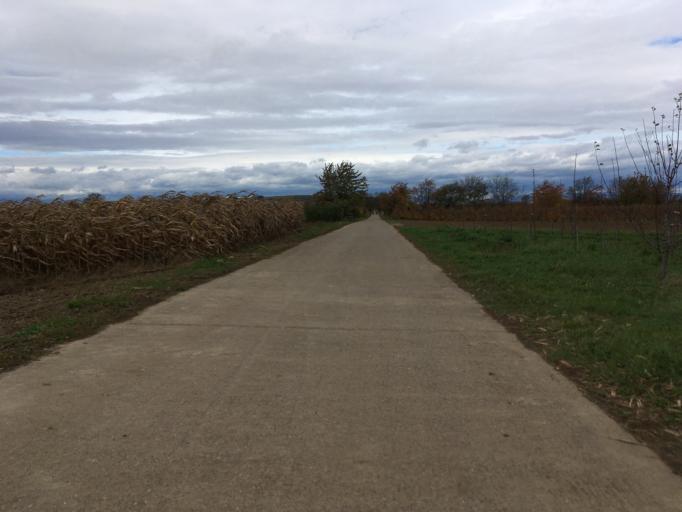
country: DE
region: Baden-Wuerttemberg
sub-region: Freiburg Region
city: Wyhl
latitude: 48.1382
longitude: 7.6502
